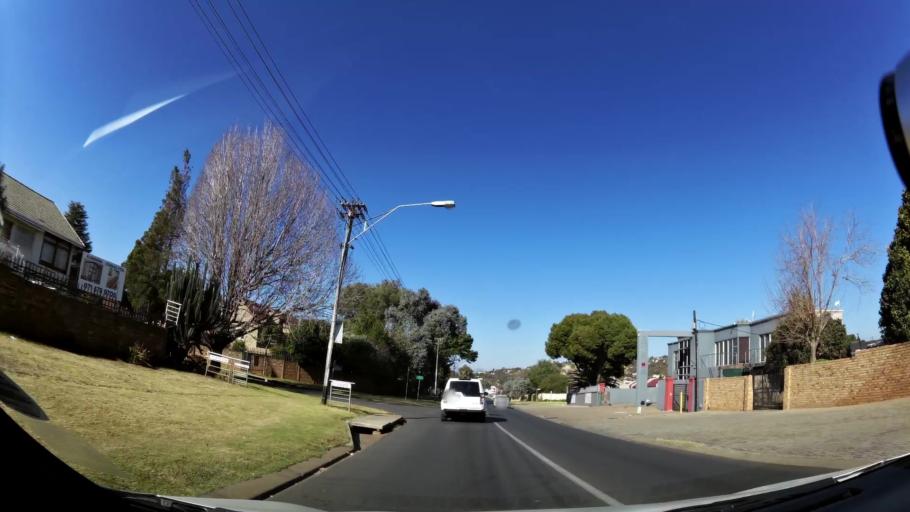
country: ZA
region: Gauteng
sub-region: City of Johannesburg Metropolitan Municipality
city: Johannesburg
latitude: -26.2702
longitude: 28.0355
